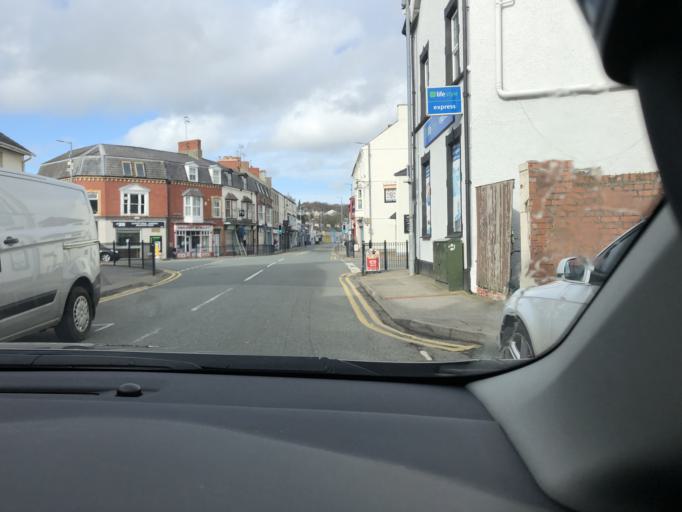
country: GB
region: Wales
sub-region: Anglesey
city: Menai Bridge
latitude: 53.2255
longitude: -4.1629
